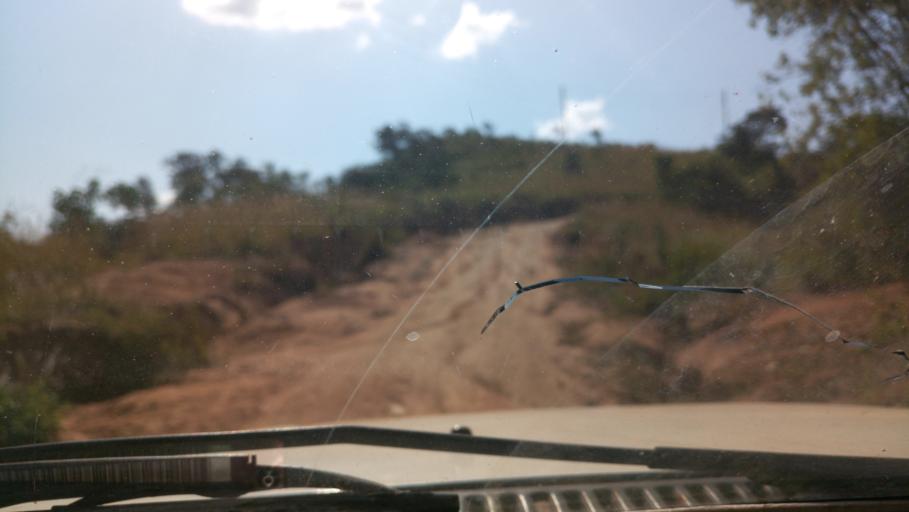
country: KE
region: Murang'a District
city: Murang'a
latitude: -0.6879
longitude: 37.1473
